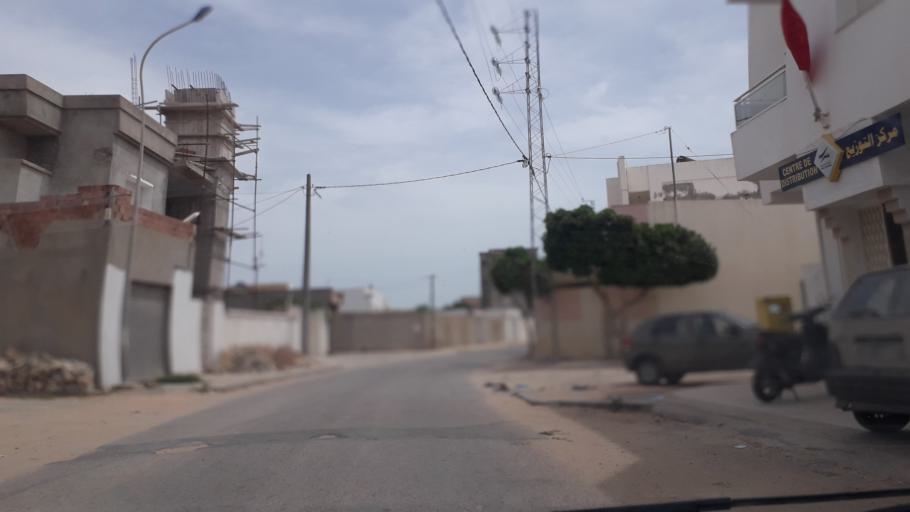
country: TN
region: Safaqis
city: Al Qarmadah
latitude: 34.8061
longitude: 10.7637
